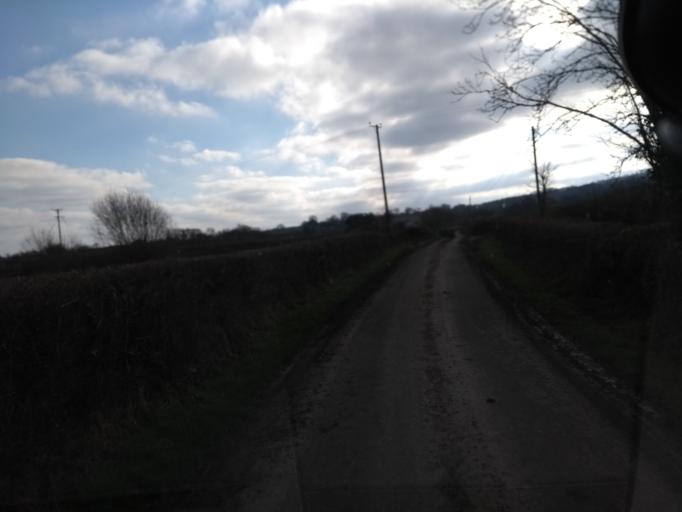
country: GB
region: England
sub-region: Somerset
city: Creech Saint Michael
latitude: 50.9610
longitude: -3.0340
